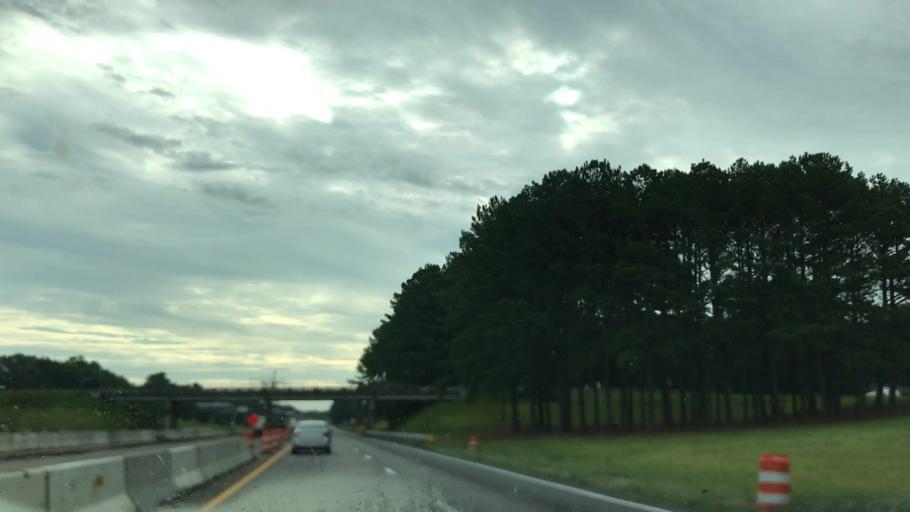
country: US
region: North Carolina
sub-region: Johnston County
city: Pine Level
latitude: 35.5481
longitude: -78.2196
